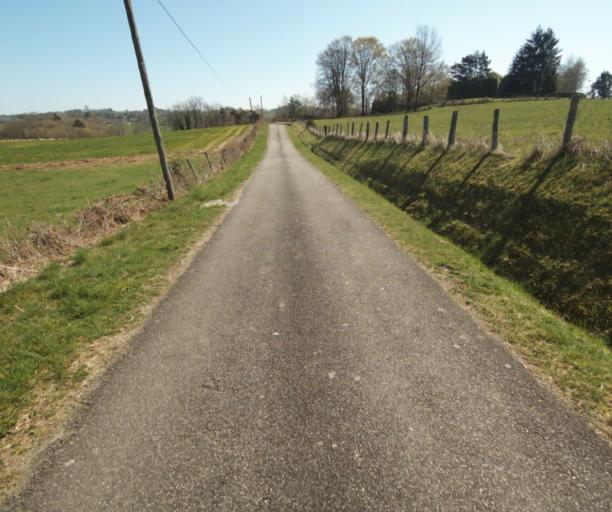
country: FR
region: Limousin
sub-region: Departement de la Correze
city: Saint-Clement
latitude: 45.3029
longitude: 1.7082
